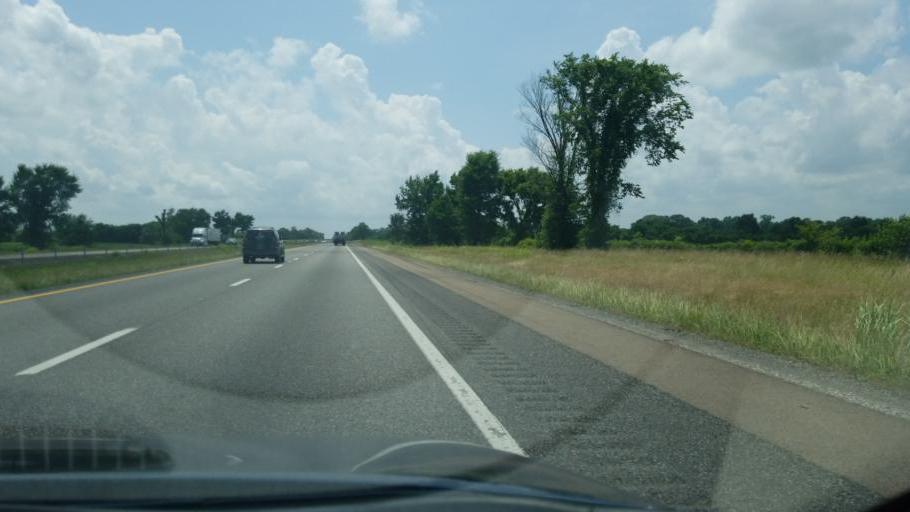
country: US
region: Tennessee
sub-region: Madison County
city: Jackson
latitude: 35.6364
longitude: -88.9382
